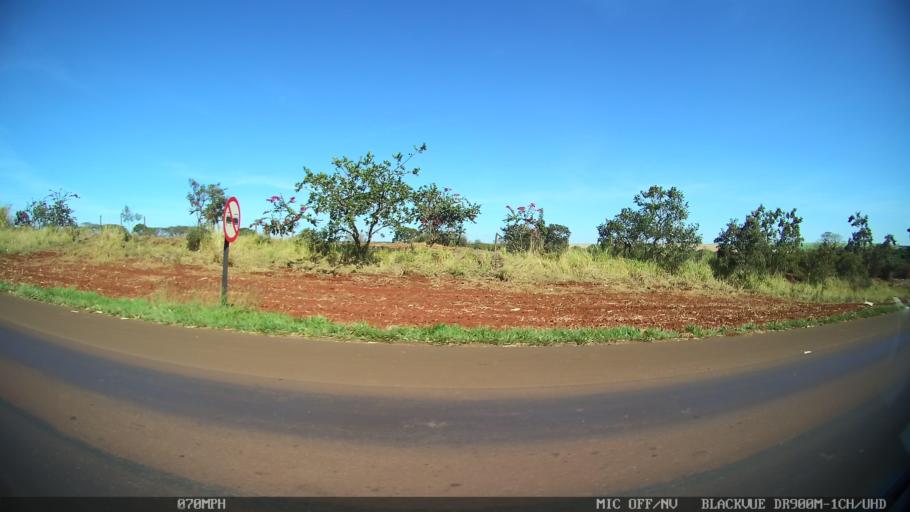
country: BR
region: Sao Paulo
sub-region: Ipua
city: Ipua
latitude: -20.4932
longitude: -47.9848
